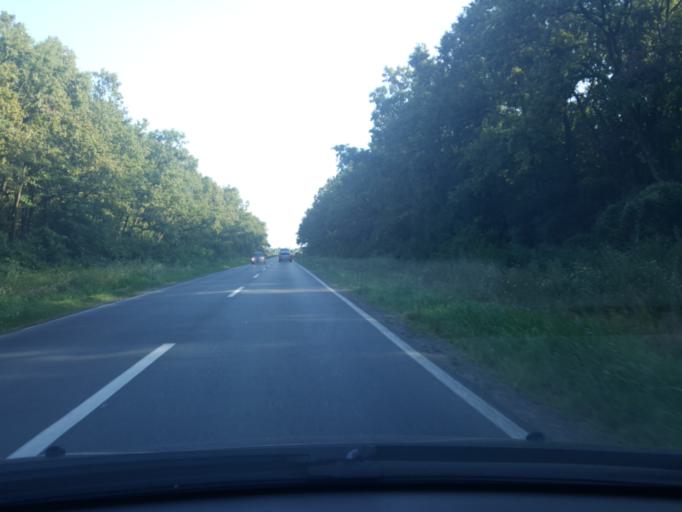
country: RS
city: Hrtkovci
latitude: 44.8981
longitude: 19.7643
